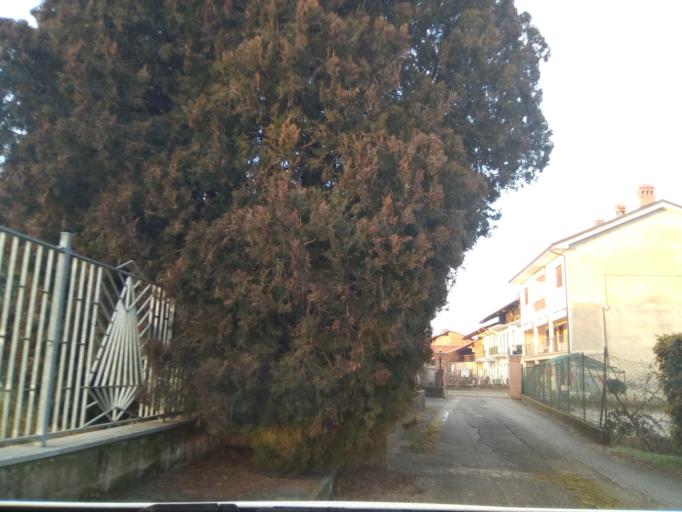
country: IT
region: Piedmont
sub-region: Provincia di Torino
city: Pavone Canavese
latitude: 45.4292
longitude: 7.8813
